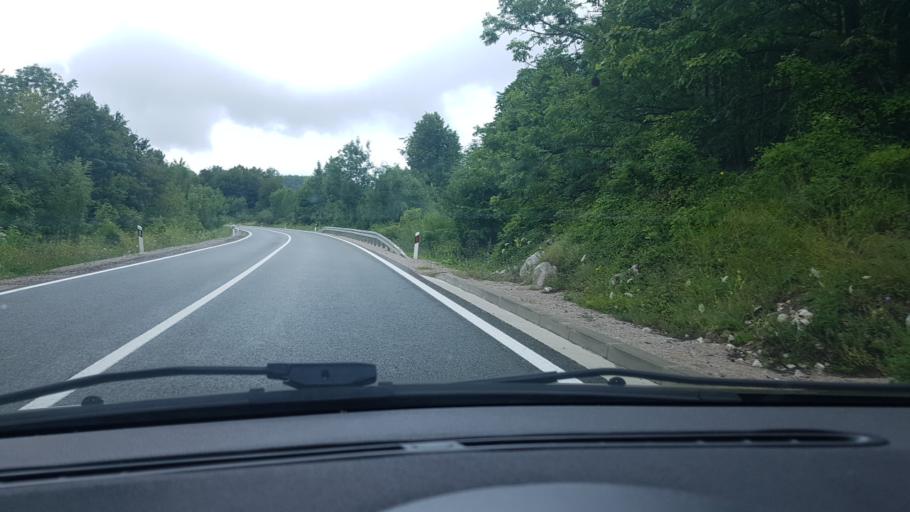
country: HR
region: Licko-Senjska
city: Jezerce
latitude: 44.8418
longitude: 15.6734
